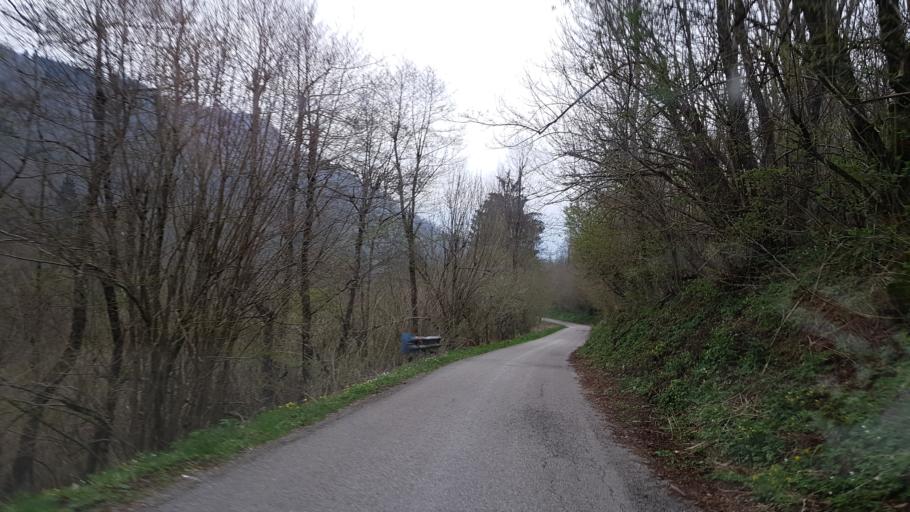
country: IT
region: Friuli Venezia Giulia
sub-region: Provincia di Udine
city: Faedis
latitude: 46.1875
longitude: 13.3951
